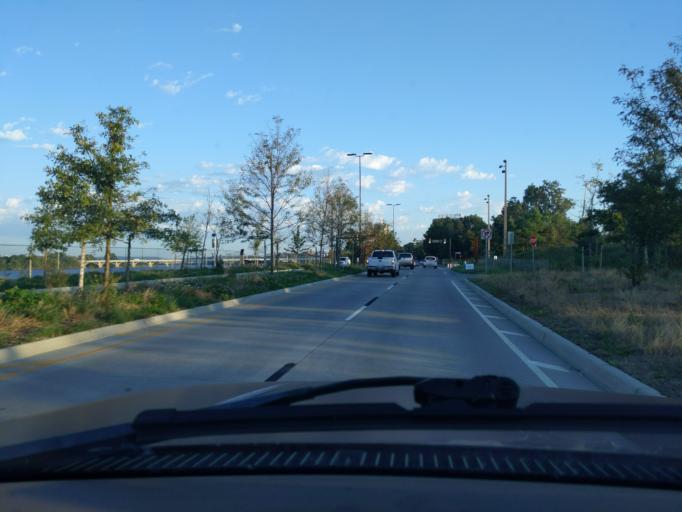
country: US
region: Oklahoma
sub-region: Tulsa County
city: Tulsa
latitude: 36.1243
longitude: -95.9865
